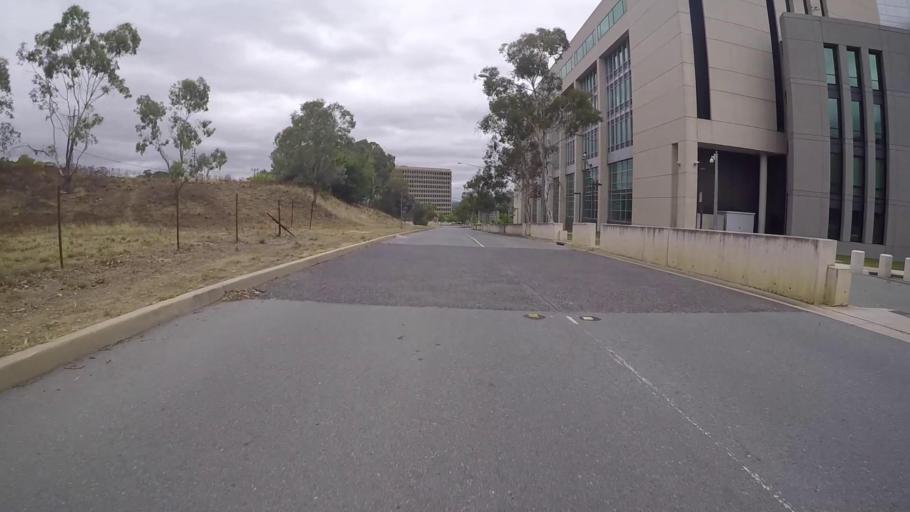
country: AU
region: Australian Capital Territory
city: Canberra
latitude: -35.2976
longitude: 149.1533
